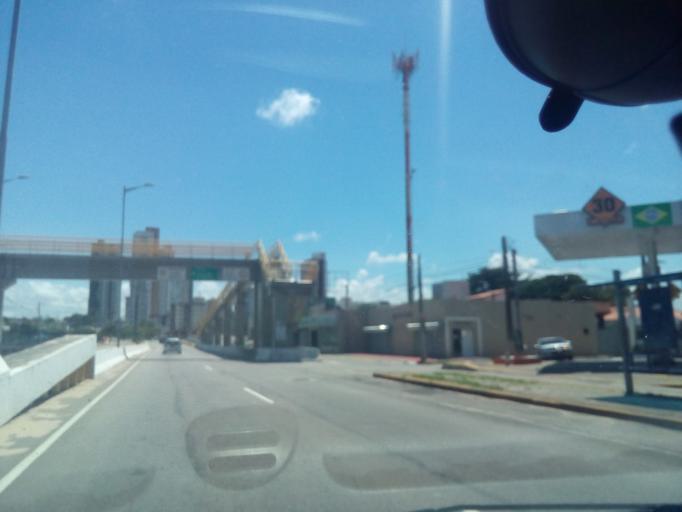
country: BR
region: Rio Grande do Norte
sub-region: Natal
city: Natal
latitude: -5.8256
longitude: -35.2158
